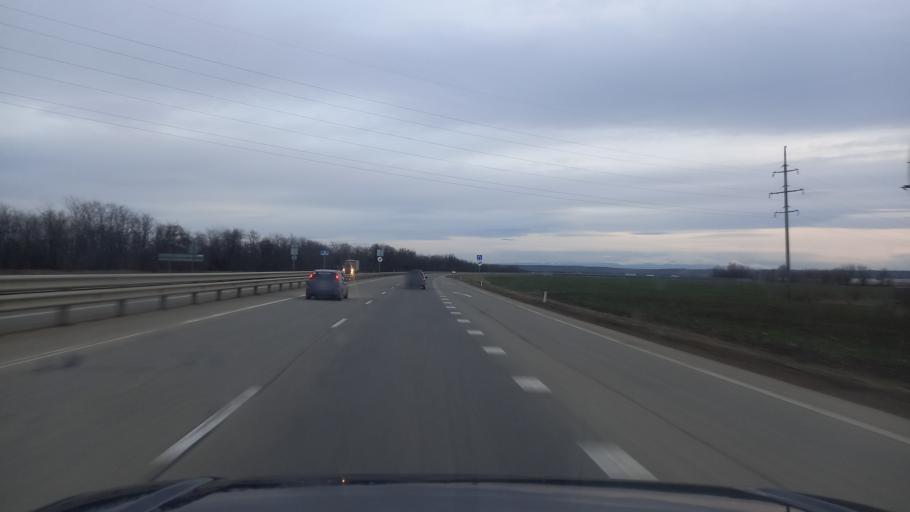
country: RU
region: Adygeya
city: Khanskaya
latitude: 44.6771
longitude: 39.9911
